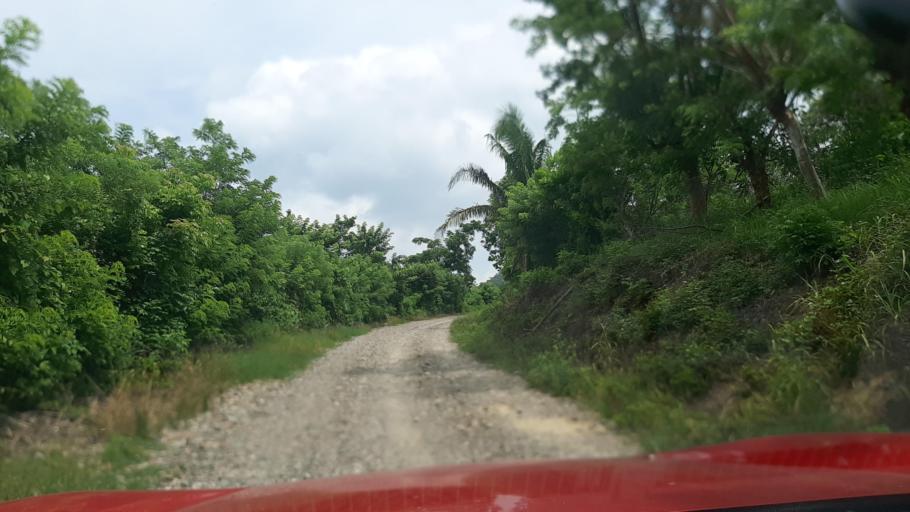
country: MX
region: Veracruz
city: Gutierrez Zamora
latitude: 20.4520
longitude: -97.1768
